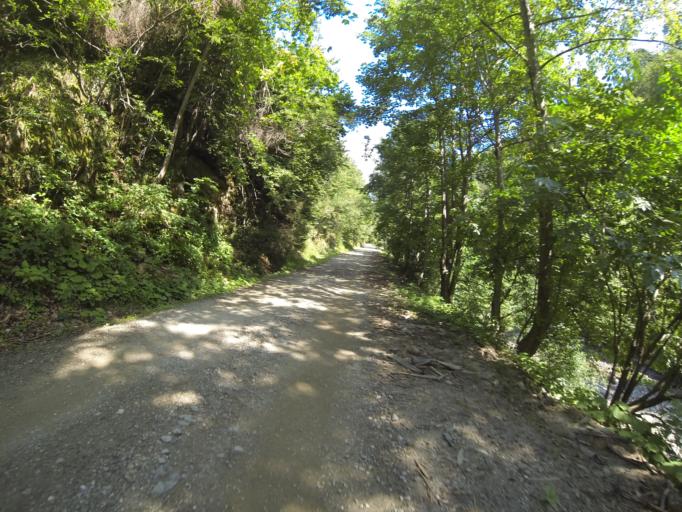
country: RO
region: Valcea
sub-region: Comuna Costesti
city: Bistrita
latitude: 45.2454
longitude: 23.9953
